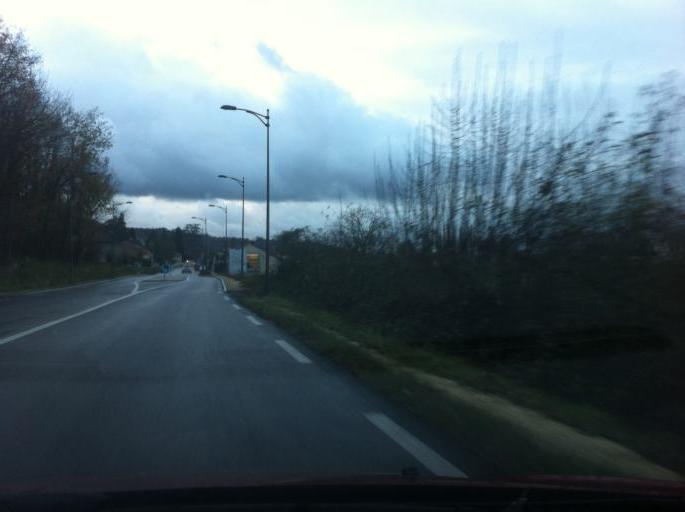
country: FR
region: Aquitaine
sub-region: Departement de la Dordogne
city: Chancelade
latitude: 45.1909
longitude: 0.6807
